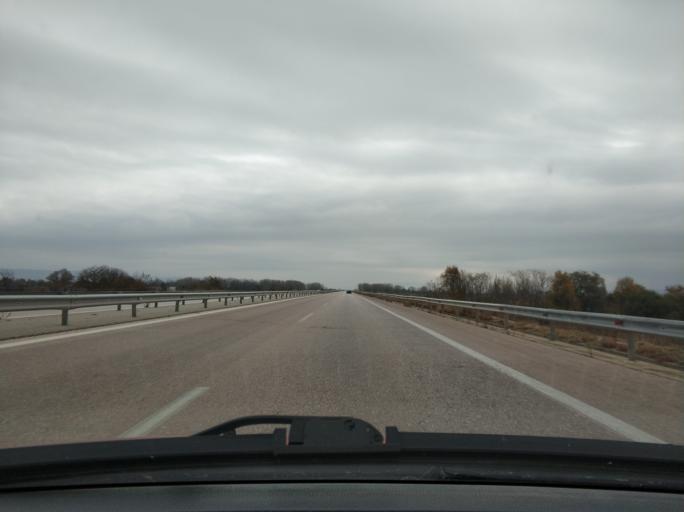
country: GR
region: Central Macedonia
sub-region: Nomos Thessalonikis
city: Kavallari
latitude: 40.7323
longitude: 23.0495
